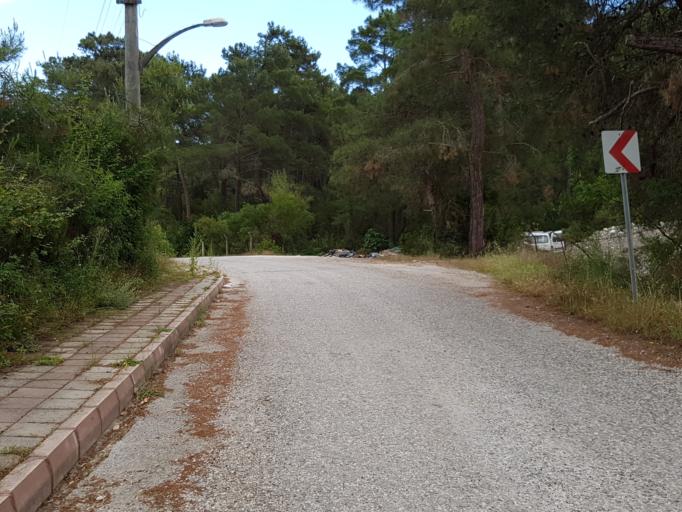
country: TR
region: Antalya
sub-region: Kemer
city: Goeynuek
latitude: 36.6431
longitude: 30.5519
